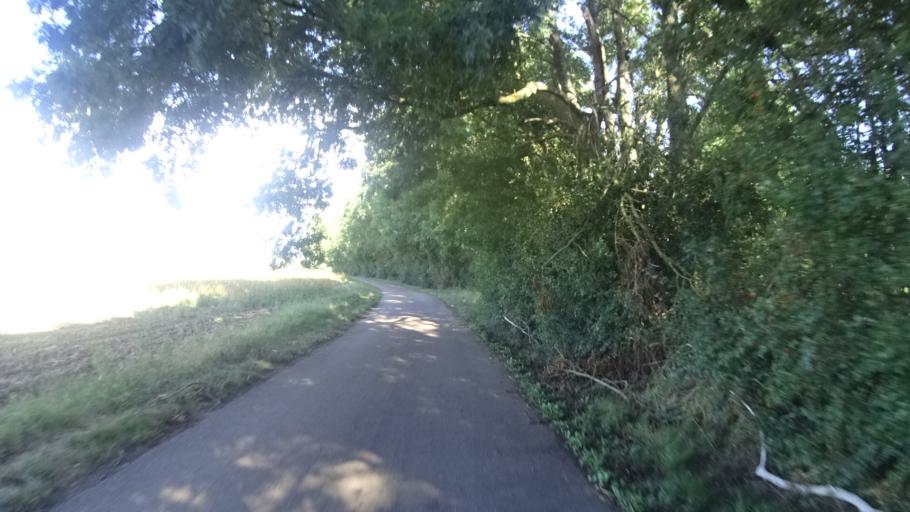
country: FR
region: Bourgogne
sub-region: Departement de la Nievre
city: Pouilly-sur-Loire
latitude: 47.3068
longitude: 2.8981
